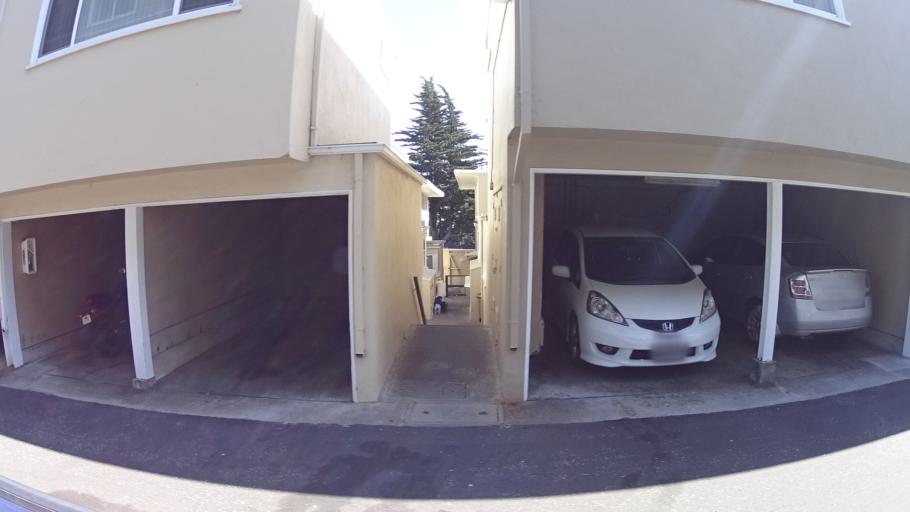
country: US
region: California
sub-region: San Mateo County
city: Broadmoor
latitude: 37.7026
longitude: -122.4865
